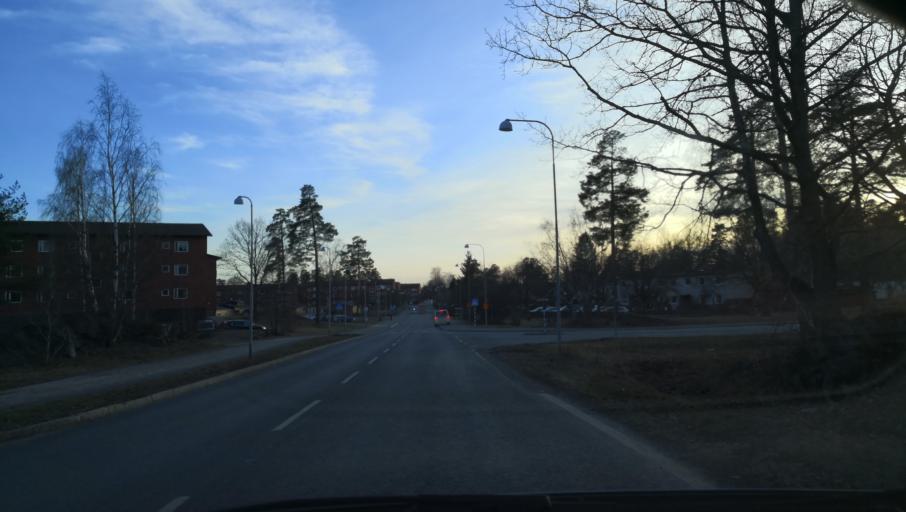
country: SE
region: Stockholm
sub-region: Varmdo Kommun
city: Gustavsberg
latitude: 59.3361
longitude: 18.3948
